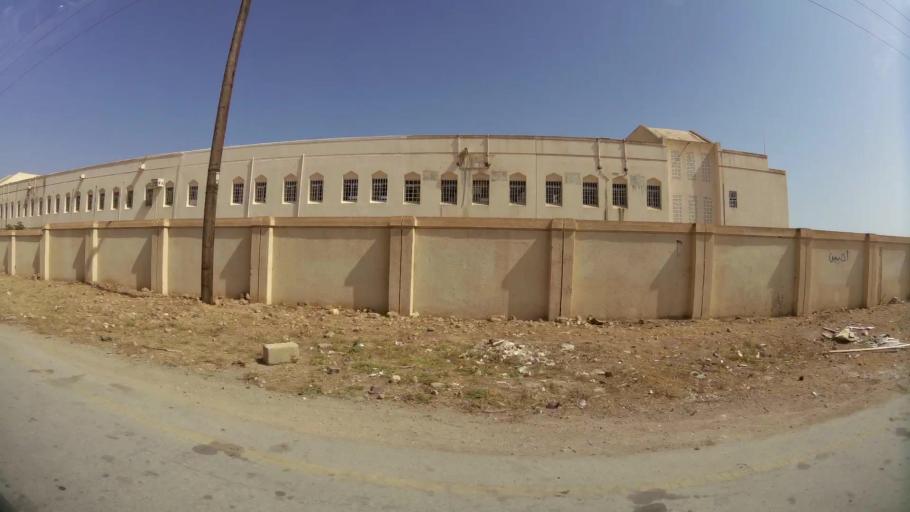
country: OM
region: Zufar
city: Salalah
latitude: 17.0447
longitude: 54.1536
